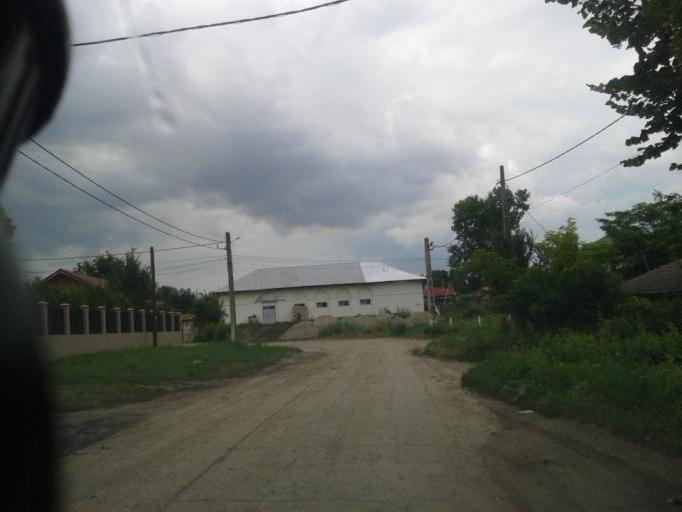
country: RO
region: Ialomita
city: Dragoesti-Snagov
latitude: 44.5326
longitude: 26.4833
